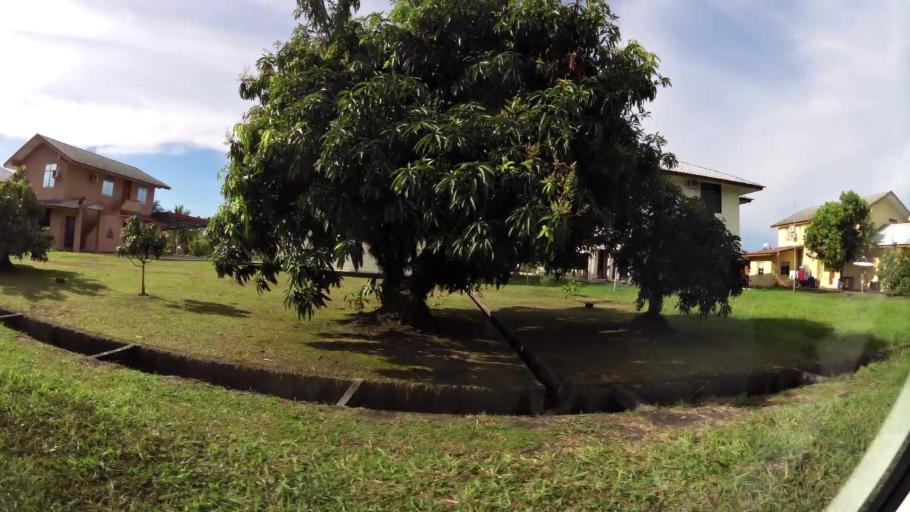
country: BN
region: Brunei and Muara
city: Bandar Seri Begawan
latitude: 4.9699
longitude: 115.0239
